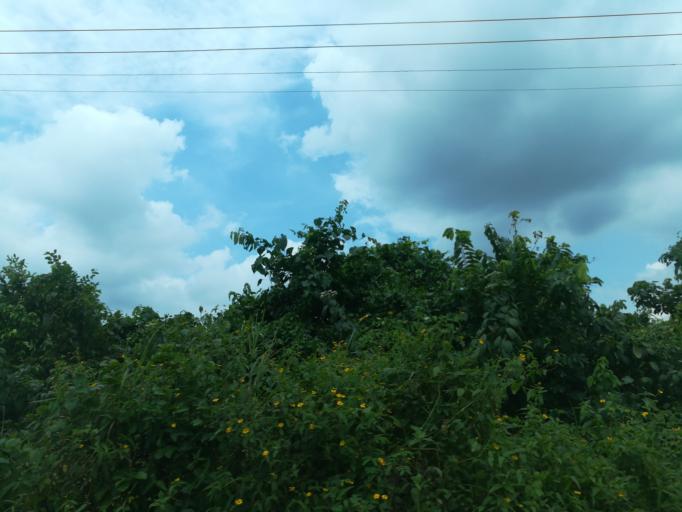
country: NG
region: Ogun
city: Odogbolu
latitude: 6.6667
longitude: 3.7100
